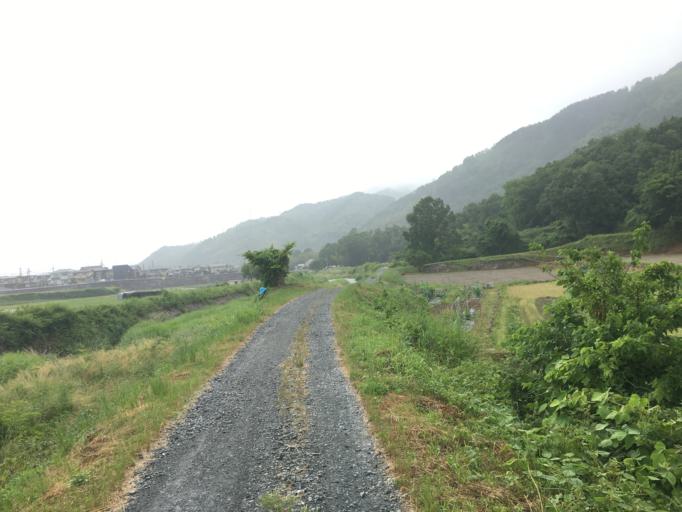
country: JP
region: Kyoto
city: Kameoka
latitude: 35.0063
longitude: 135.6129
